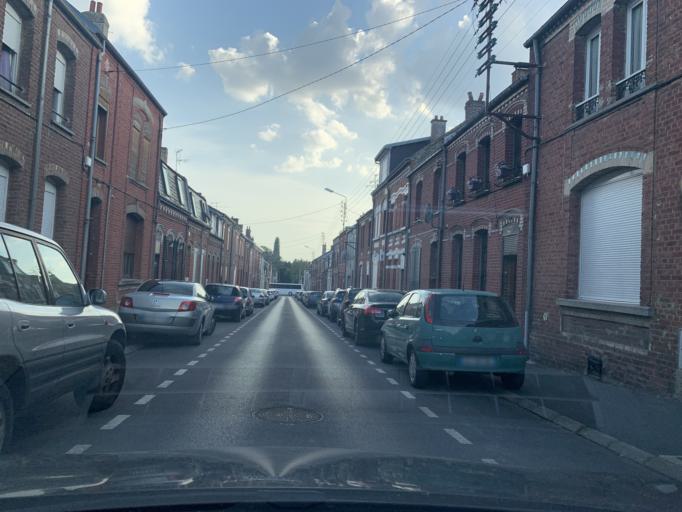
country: FR
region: Nord-Pas-de-Calais
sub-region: Departement du Nord
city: Caudry
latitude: 50.1286
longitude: 3.4083
